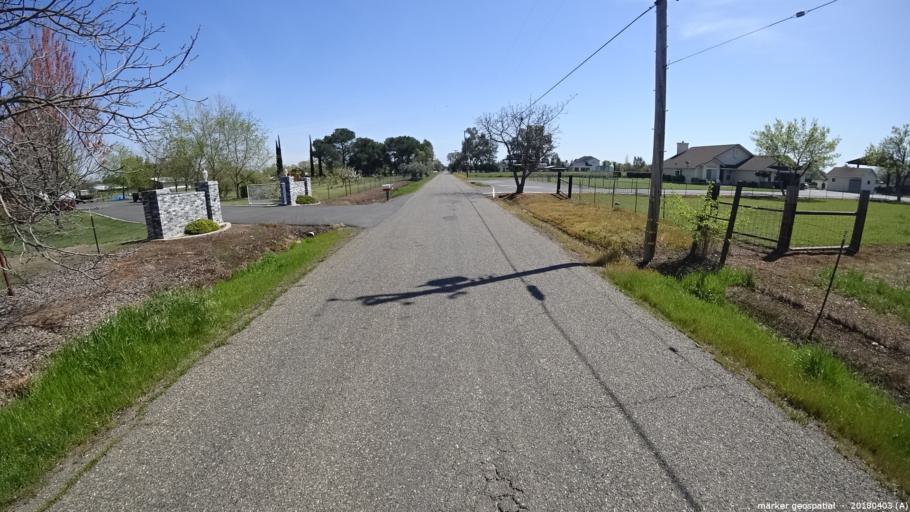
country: US
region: California
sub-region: Sacramento County
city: Wilton
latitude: 38.4021
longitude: -121.2728
